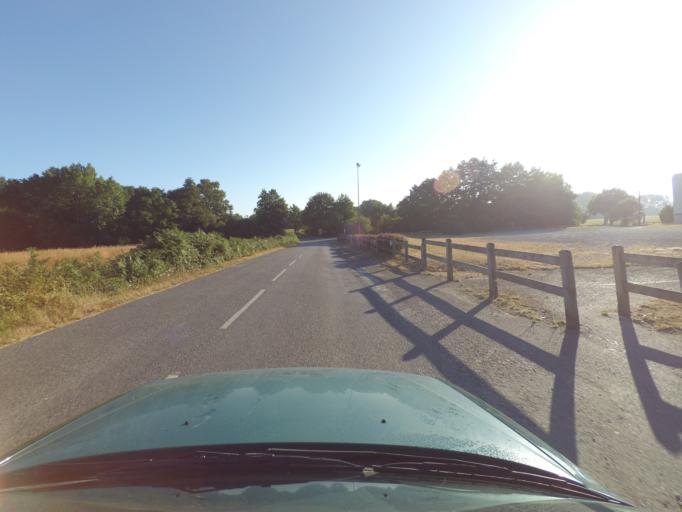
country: FR
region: Pays de la Loire
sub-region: Departement de la Loire-Atlantique
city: Montbert
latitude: 47.0618
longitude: -1.4816
